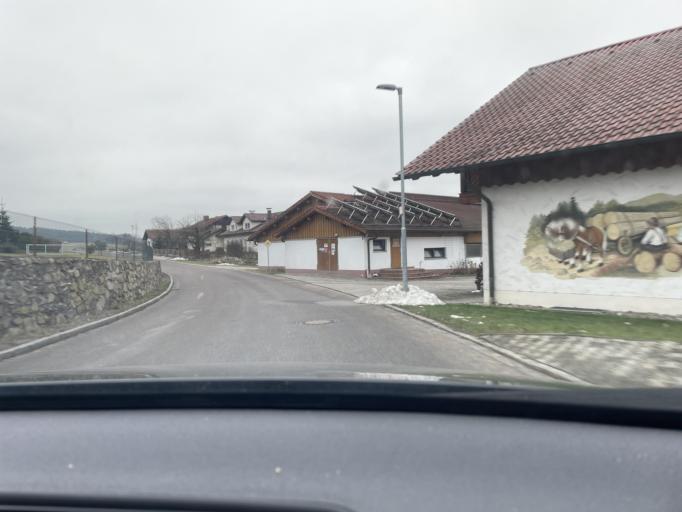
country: DE
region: Bavaria
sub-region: Upper Palatinate
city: Cham
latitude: 49.1928
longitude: 12.6897
